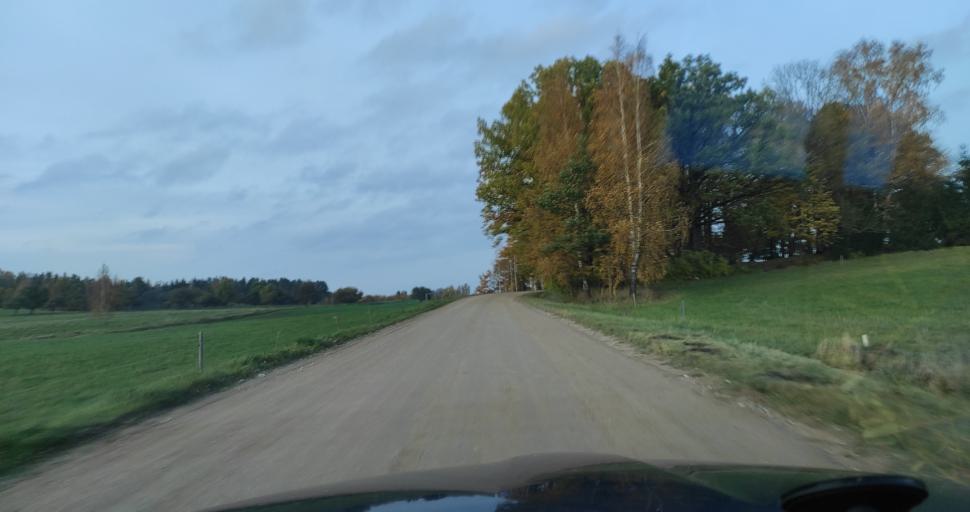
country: LV
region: Aizpute
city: Aizpute
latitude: 56.6551
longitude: 21.7948
